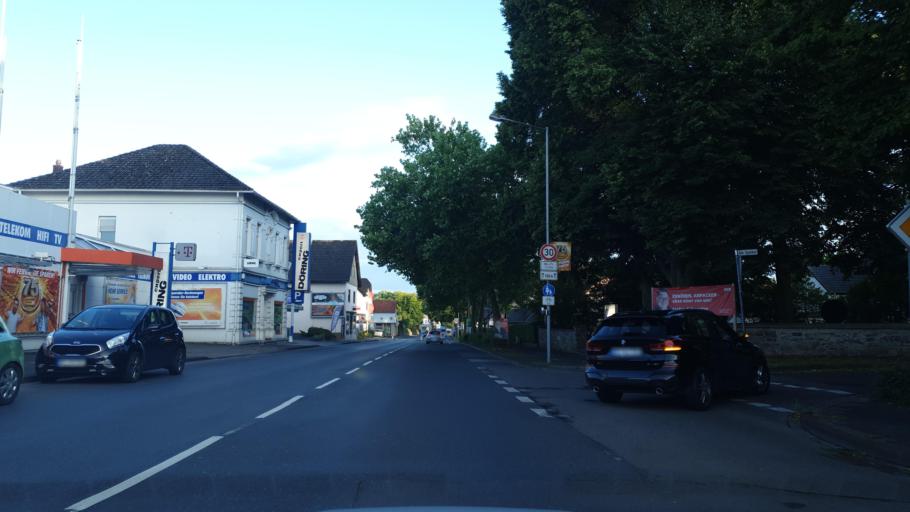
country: DE
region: North Rhine-Westphalia
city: Loehne
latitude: 52.2188
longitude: 8.7090
